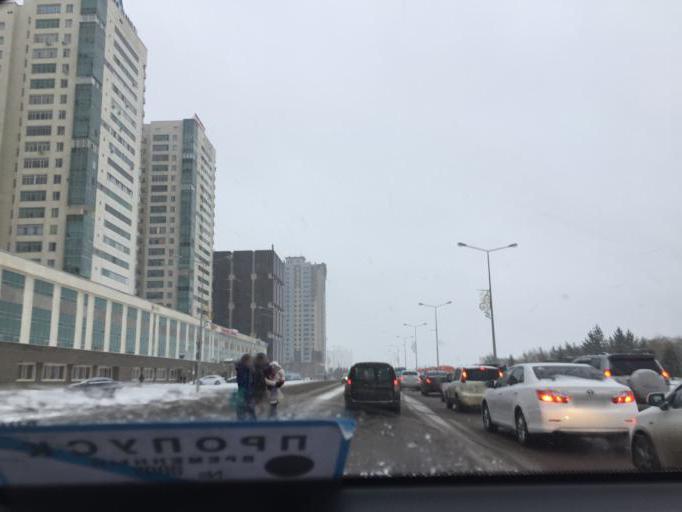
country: KZ
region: Astana Qalasy
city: Astana
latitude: 51.1326
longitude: 71.4594
